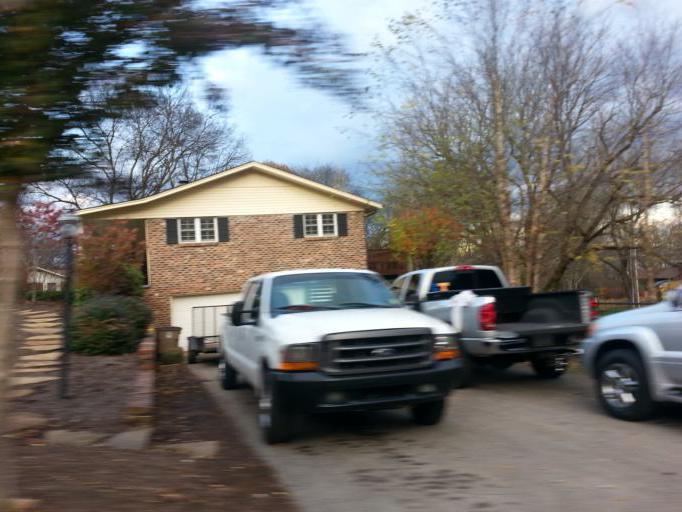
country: US
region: Tennessee
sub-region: Knox County
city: Knoxville
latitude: 35.9283
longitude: -84.0160
